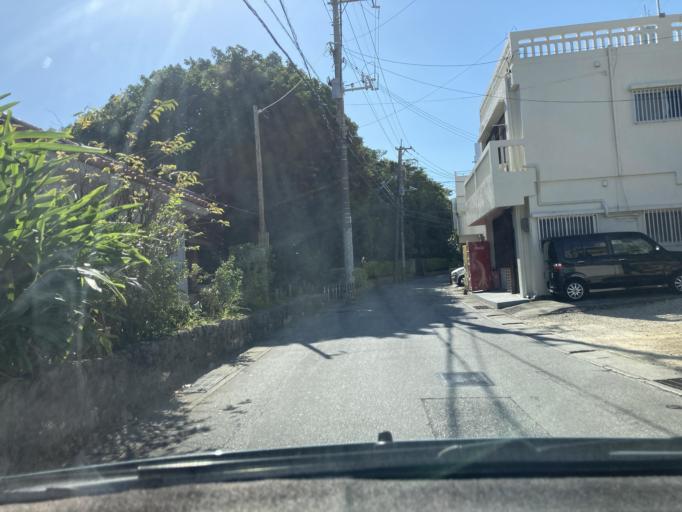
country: JP
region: Okinawa
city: Naha-shi
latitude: 26.2053
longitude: 127.7148
